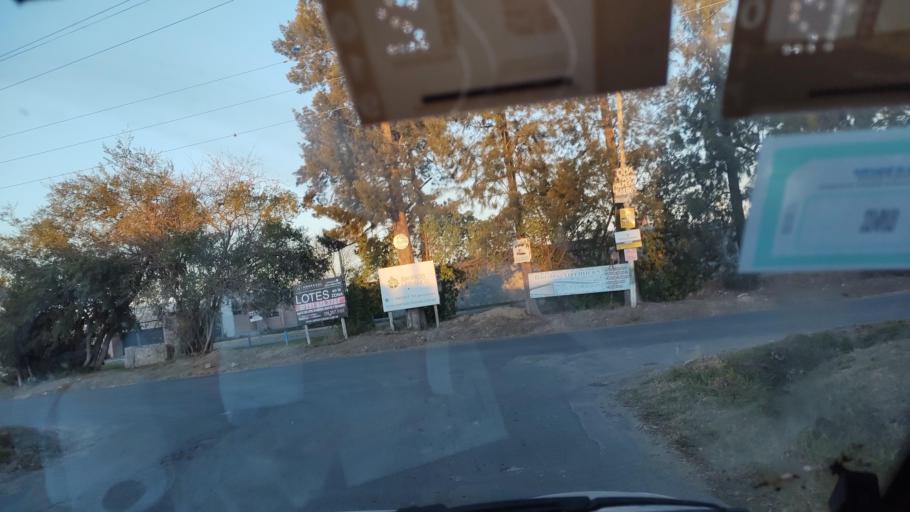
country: AR
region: Buenos Aires
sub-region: Partido de La Plata
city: La Plata
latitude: -34.9066
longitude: -58.0341
